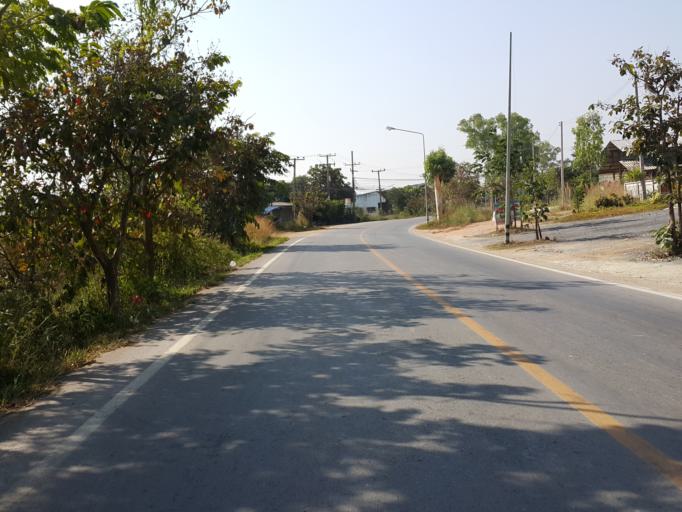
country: TH
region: Lamphun
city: Ban Thi
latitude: 18.6555
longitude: 99.1291
